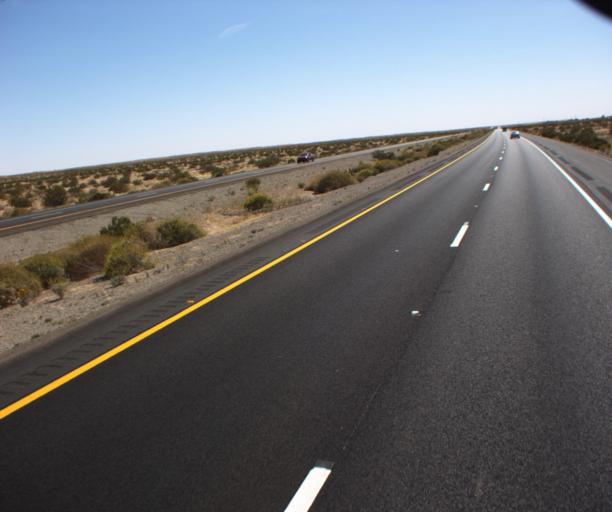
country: US
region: Arizona
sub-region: Yuma County
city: Fortuna Foothills
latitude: 32.5906
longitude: -114.5484
